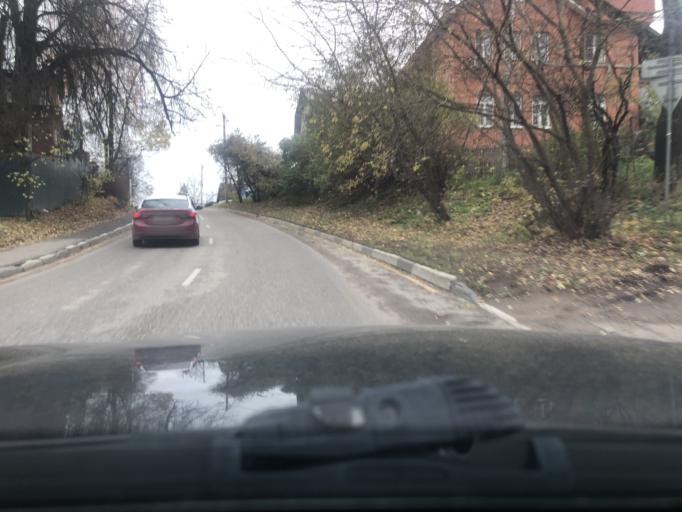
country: RU
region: Moskovskaya
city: Sergiyev Posad
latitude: 56.3143
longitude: 38.1282
